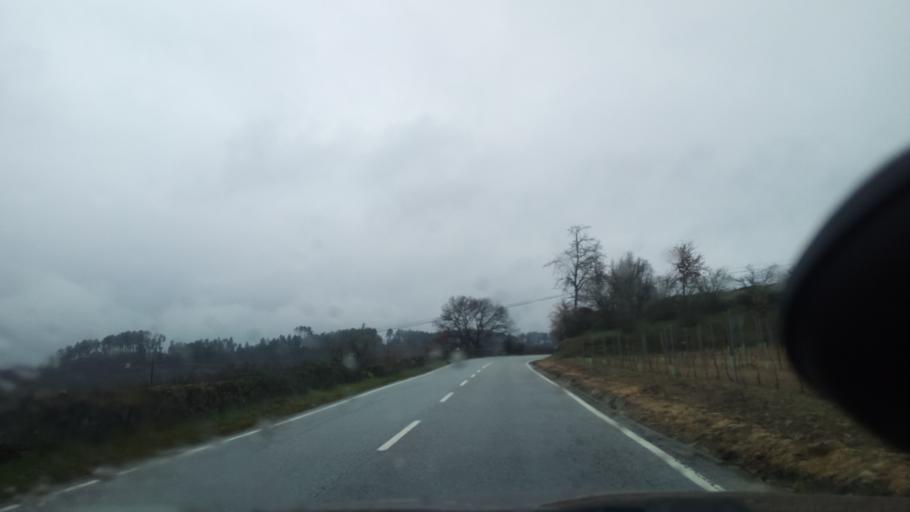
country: PT
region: Viseu
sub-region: Viseu
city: Rio de Loba
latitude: 40.6389
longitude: -7.8350
